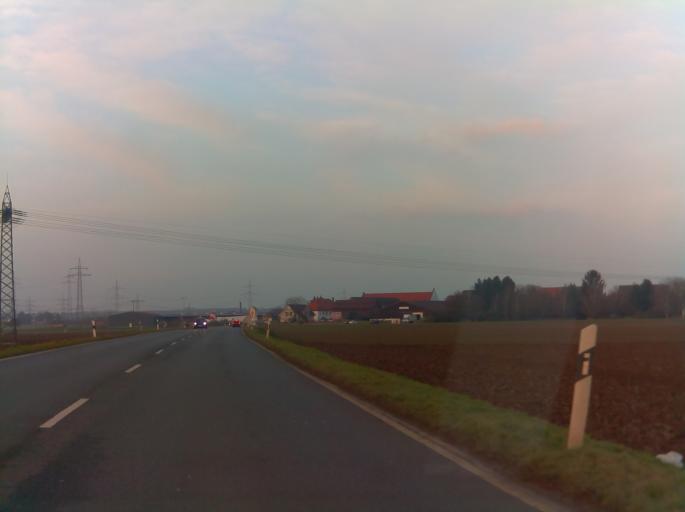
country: DE
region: Baden-Wuerttemberg
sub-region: Karlsruhe Region
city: Sandhausen
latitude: 49.3597
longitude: 8.6497
